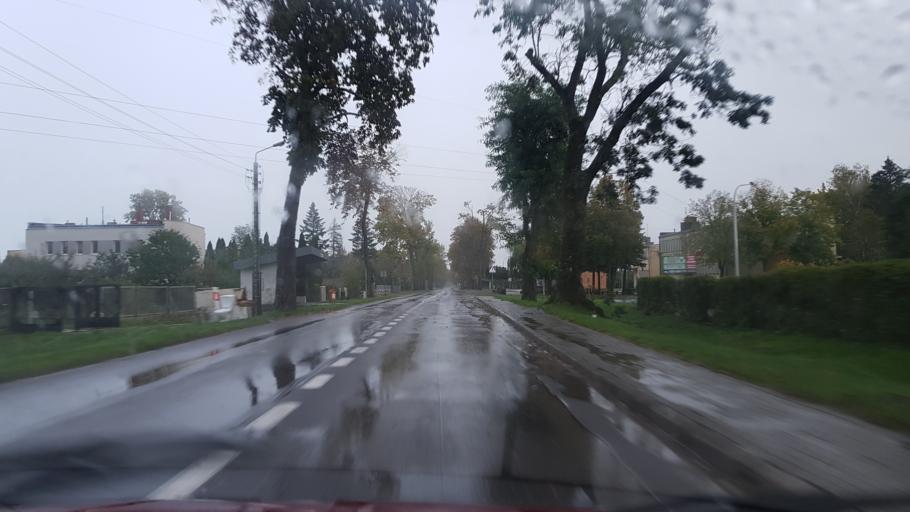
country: PL
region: Greater Poland Voivodeship
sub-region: Powiat pilski
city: Szydlowo
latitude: 53.1680
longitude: 16.5970
